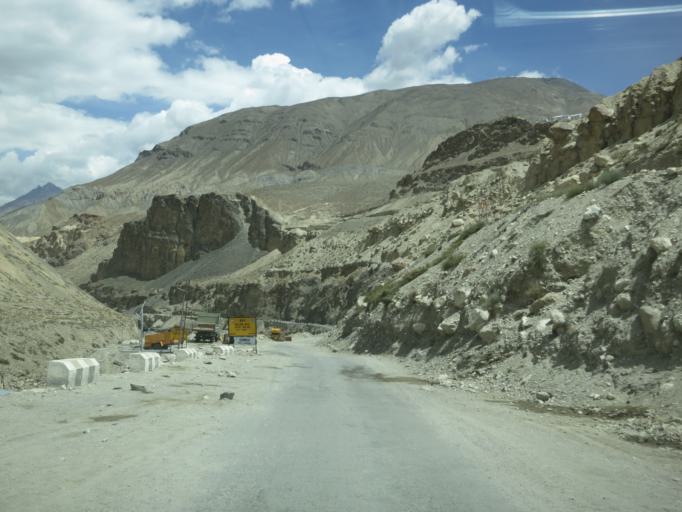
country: CN
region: Tibet Autonomous Region
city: Diyag
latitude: 32.0537
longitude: 78.6073
